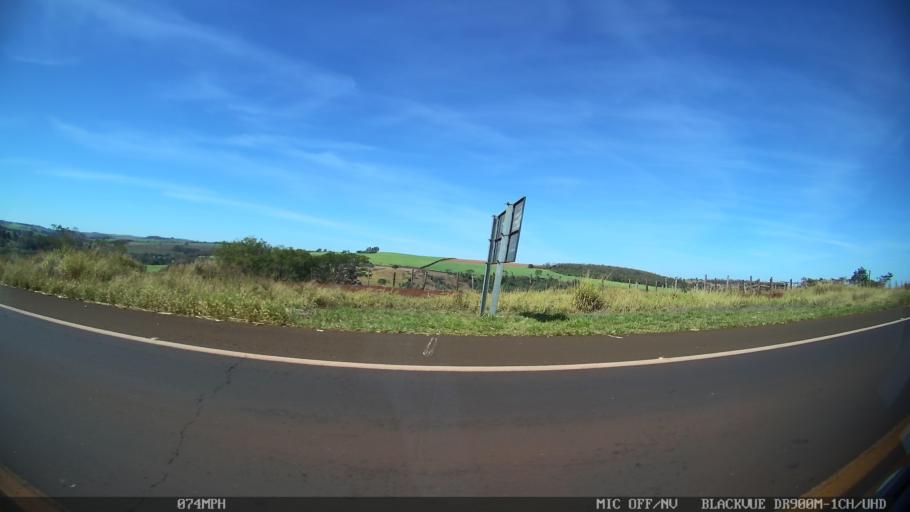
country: BR
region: Sao Paulo
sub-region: Sao Joaquim Da Barra
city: Sao Joaquim da Barra
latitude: -20.5598
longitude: -47.6833
